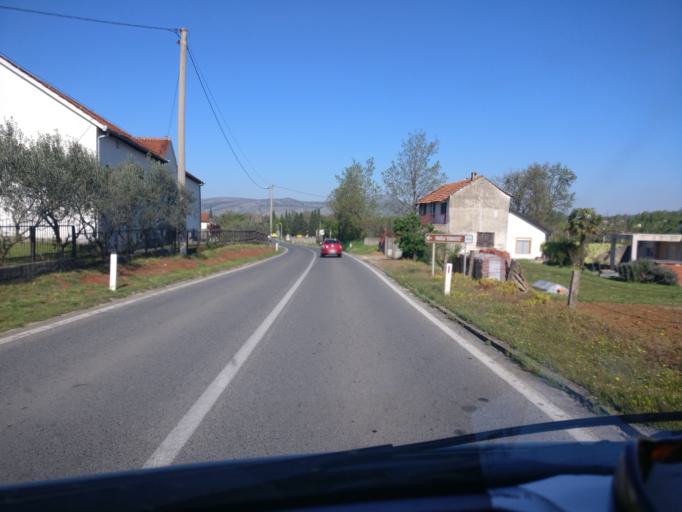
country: BA
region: Federation of Bosnia and Herzegovina
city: Tasovcici
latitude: 43.1364
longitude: 17.7860
